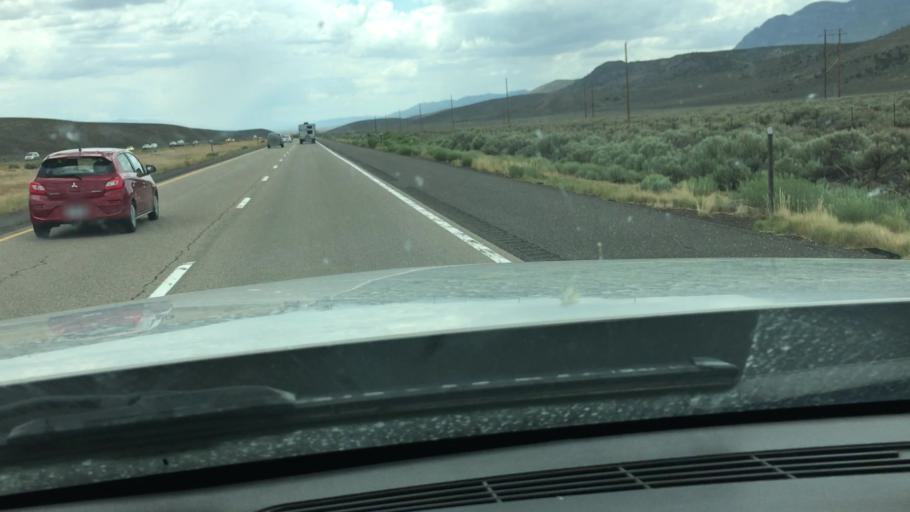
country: US
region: Utah
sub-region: Beaver County
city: Beaver
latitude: 38.1057
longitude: -112.6528
